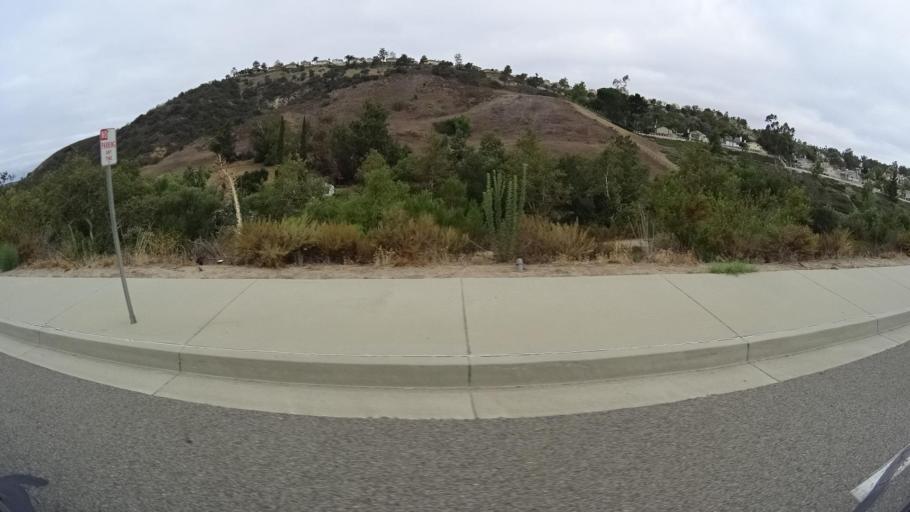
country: US
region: California
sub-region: Orange County
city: Portola Hills
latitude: 33.6764
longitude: -117.6227
